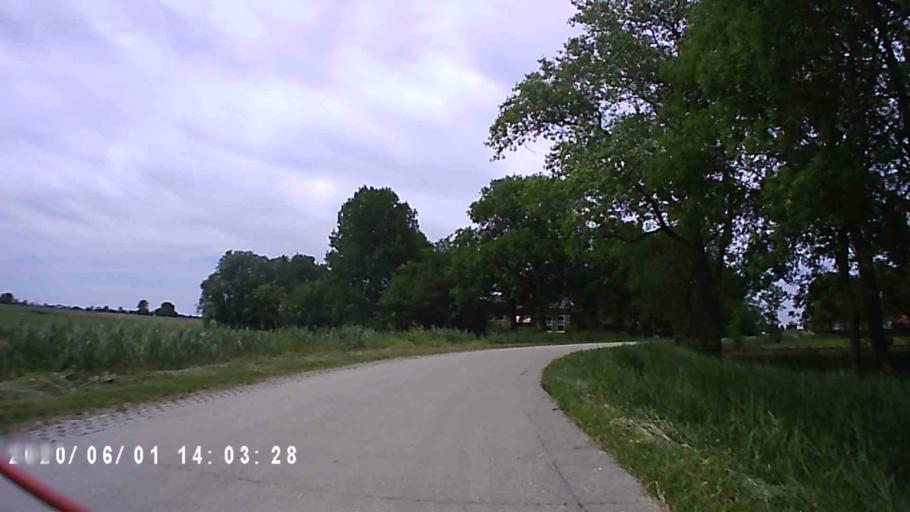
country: NL
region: Friesland
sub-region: Gemeente Littenseradiel
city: Winsum
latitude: 53.1120
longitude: 5.6359
